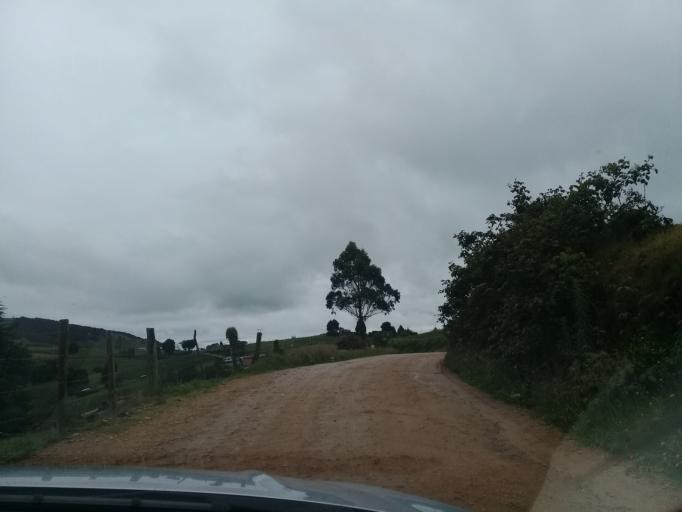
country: CO
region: Boyaca
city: Samaca
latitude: 5.4496
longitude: -73.4373
